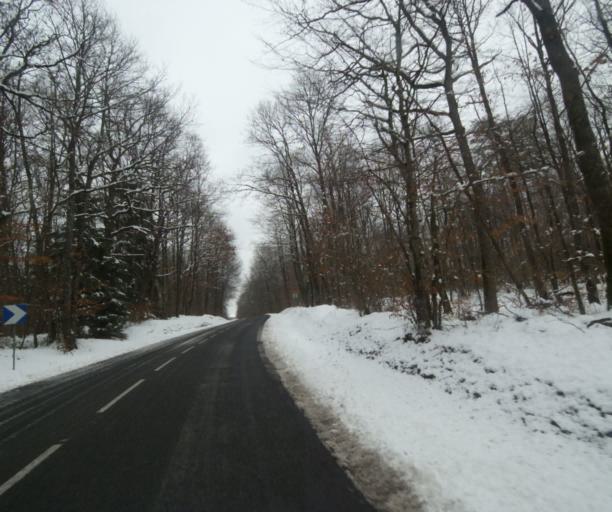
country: FR
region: Champagne-Ardenne
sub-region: Departement de la Haute-Marne
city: Laneuville-a-Remy
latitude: 48.4433
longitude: 4.8596
